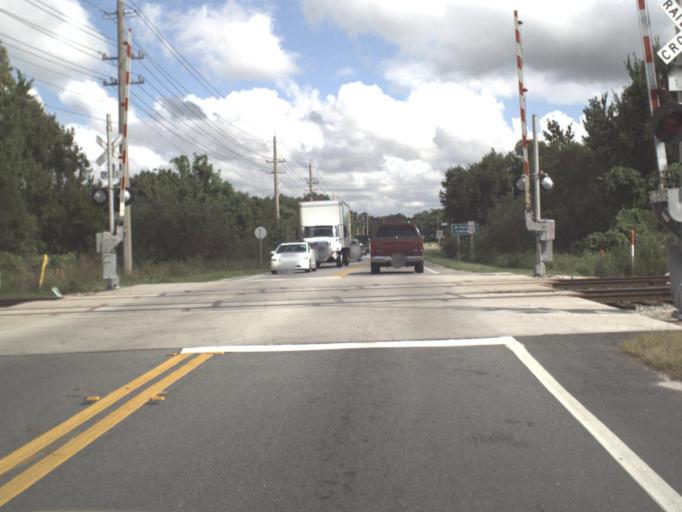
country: US
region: Florida
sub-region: Polk County
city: Winston
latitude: 28.0330
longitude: -82.0191
